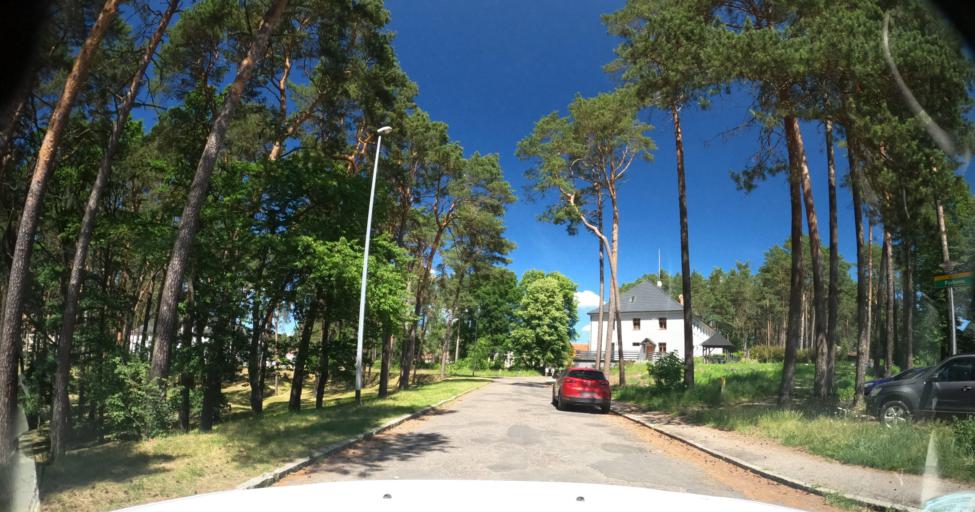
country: PL
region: West Pomeranian Voivodeship
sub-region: Powiat szczecinecki
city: Borne Sulinowo
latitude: 53.5845
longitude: 16.5481
